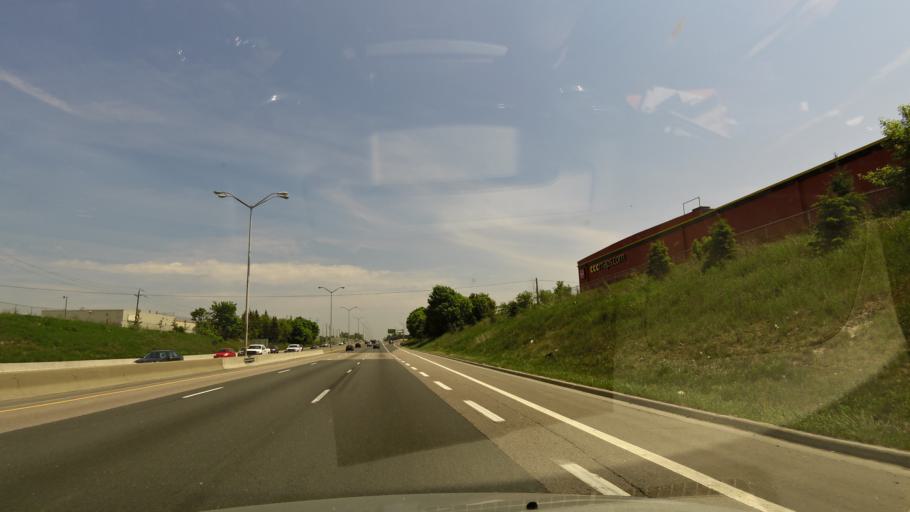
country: CA
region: Ontario
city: Oshawa
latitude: 43.8819
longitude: -78.8540
